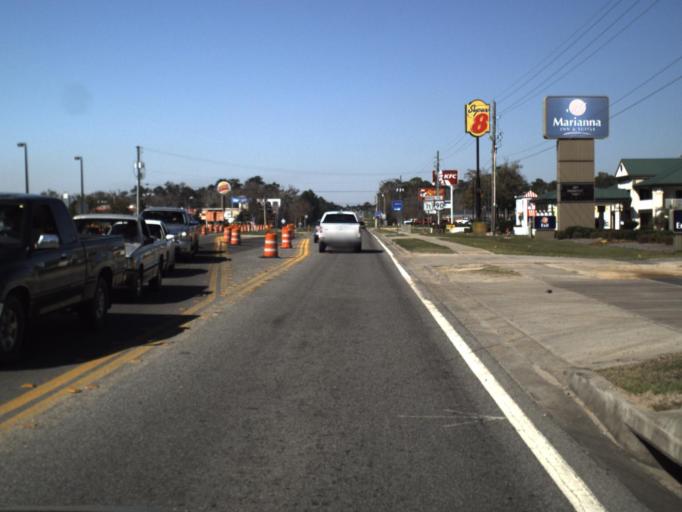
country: US
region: Florida
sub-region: Jackson County
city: Marianna
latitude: 30.7261
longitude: -85.1853
